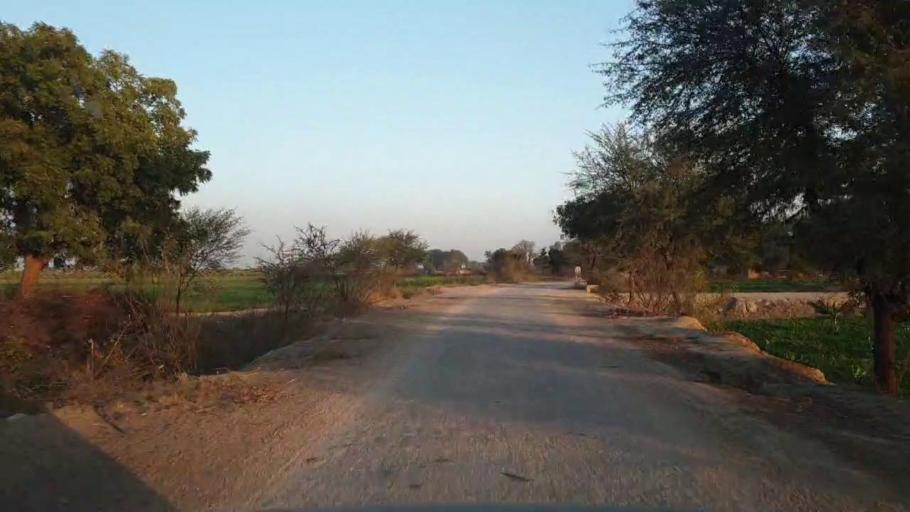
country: PK
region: Sindh
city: Tando Jam
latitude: 25.3031
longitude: 68.6389
